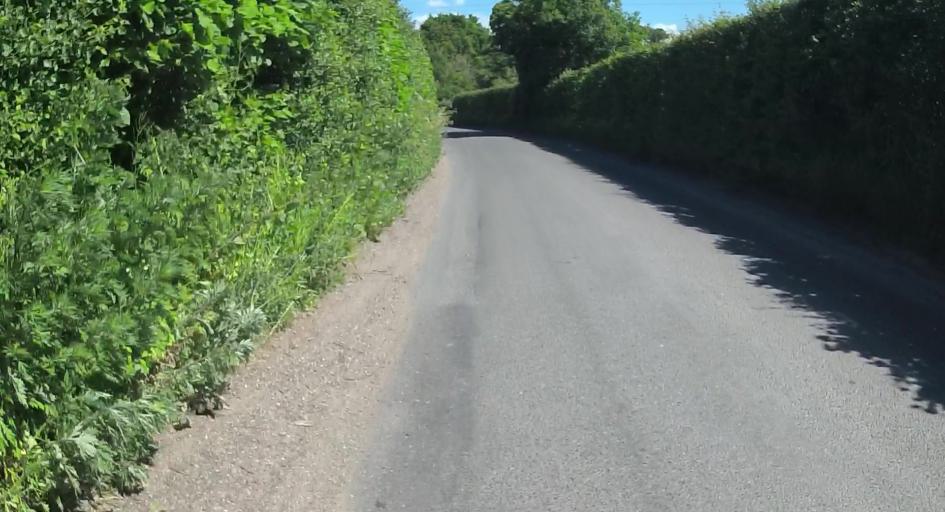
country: GB
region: England
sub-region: Hampshire
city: Hook
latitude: 51.3137
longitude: -0.9975
